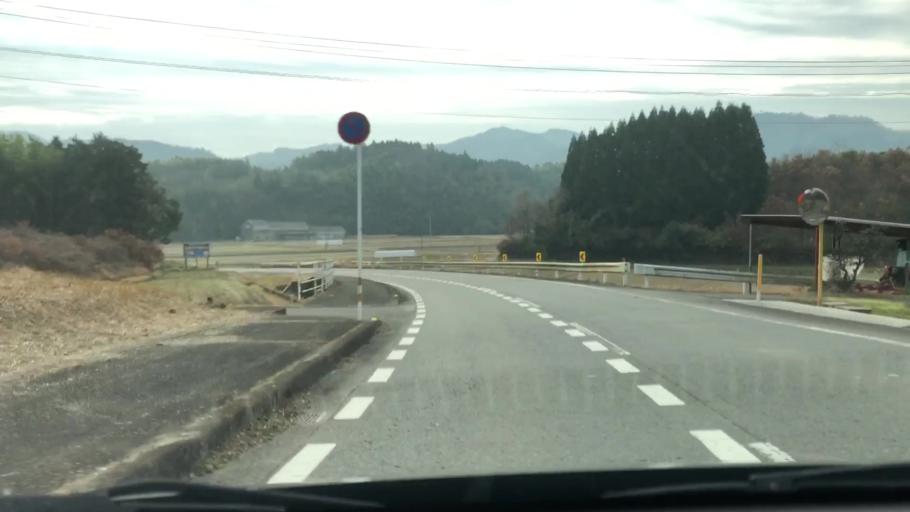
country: JP
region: Oita
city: Takedamachi
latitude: 32.9754
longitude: 131.5596
